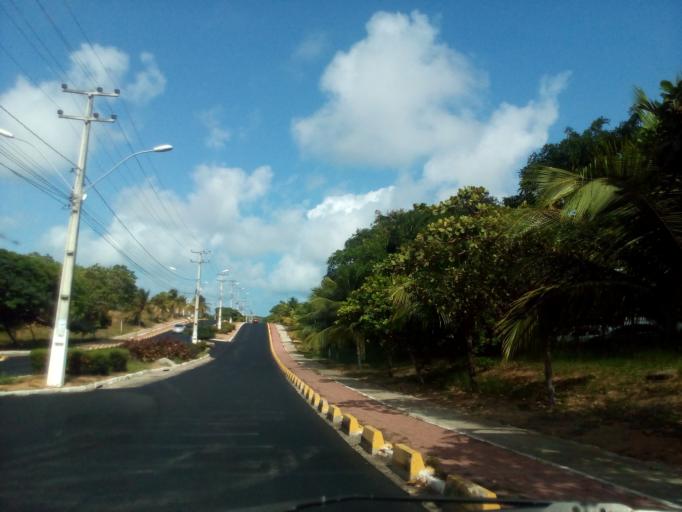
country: BR
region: Rio Grande do Norte
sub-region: Natal
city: Natal
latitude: -5.8383
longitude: -35.2093
